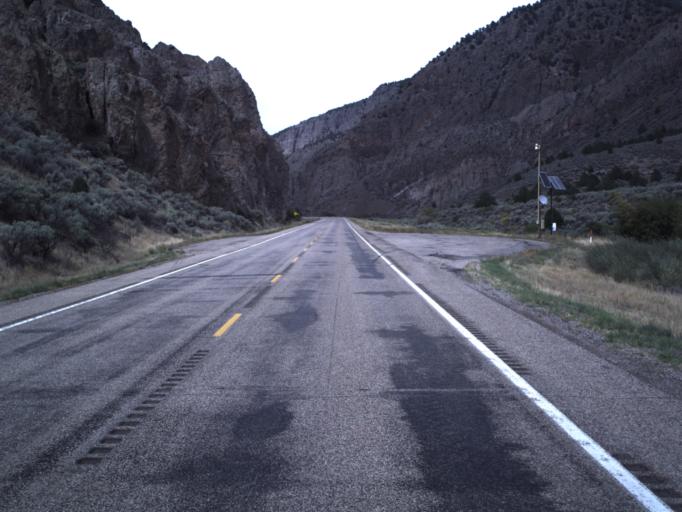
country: US
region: Utah
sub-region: Piute County
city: Junction
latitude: 38.0958
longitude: -112.3369
